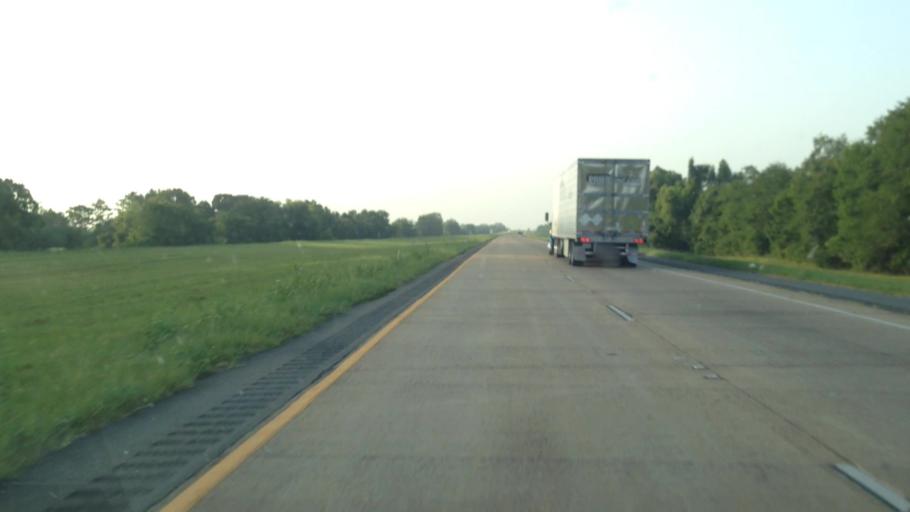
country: US
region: Louisiana
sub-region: Natchitoches Parish
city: Vienna Bend
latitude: 31.6347
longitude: -93.0740
